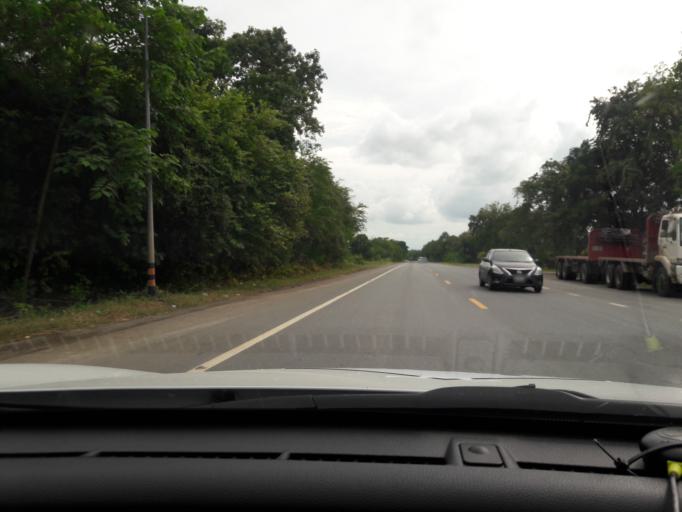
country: TH
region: Nakhon Sawan
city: Tak Fa
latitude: 15.3915
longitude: 100.5089
